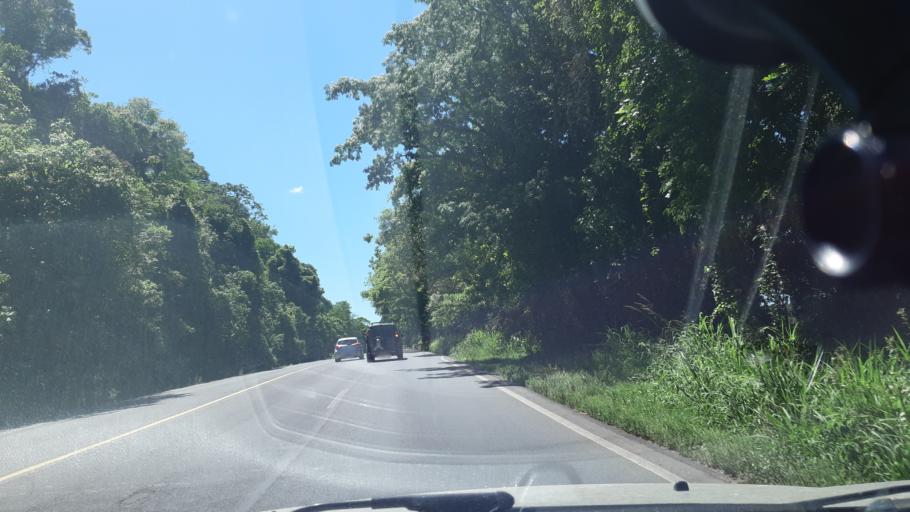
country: BR
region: Rio Grande do Sul
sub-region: Estancia Velha
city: Estancia Velha
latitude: -29.6283
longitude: -51.1426
